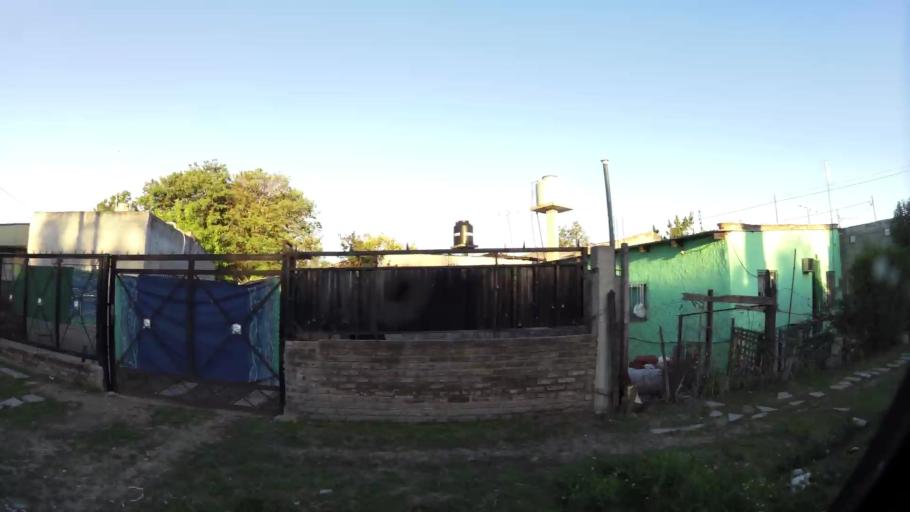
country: AR
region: Buenos Aires
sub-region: Partido de Almirante Brown
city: Adrogue
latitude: -34.7854
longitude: -58.3364
